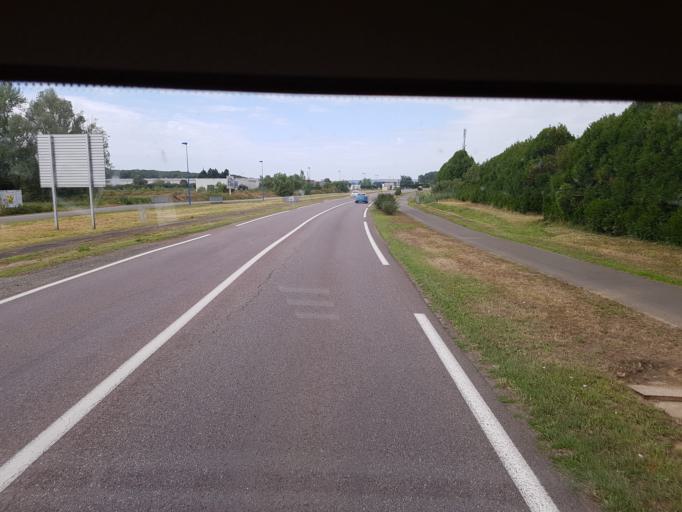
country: FR
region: Lorraine
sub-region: Departement de la Moselle
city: Basse-Ham
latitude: 49.3789
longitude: 6.2336
